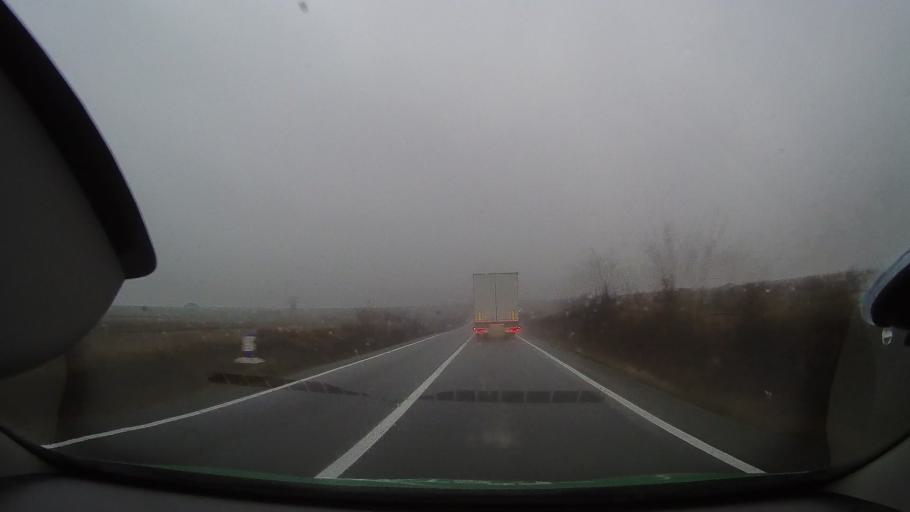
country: RO
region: Bihor
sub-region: Comuna Olcea
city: Calacea
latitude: 46.6551
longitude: 21.9602
